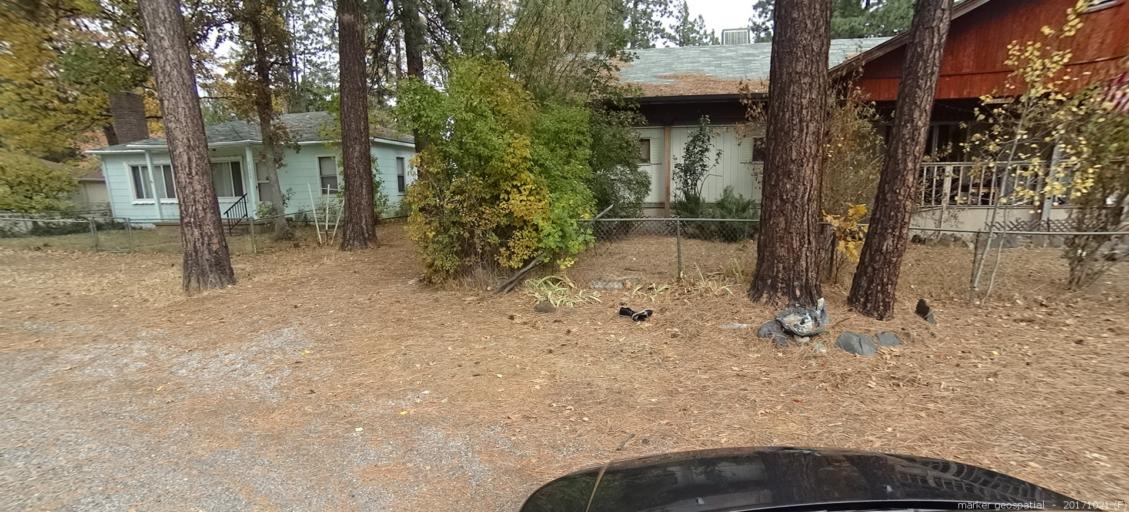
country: US
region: California
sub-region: Shasta County
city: Burney
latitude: 40.9165
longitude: -121.6244
